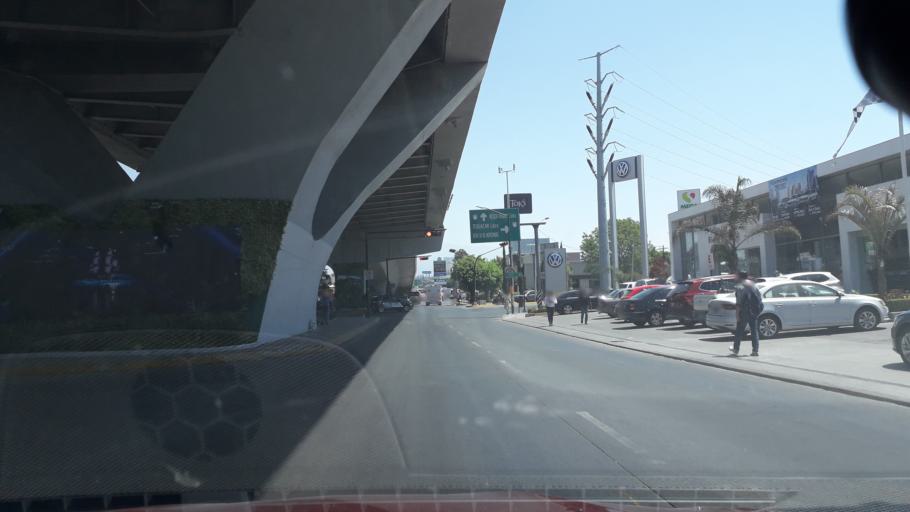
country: MX
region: Puebla
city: Puebla
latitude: 19.0640
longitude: -98.1802
